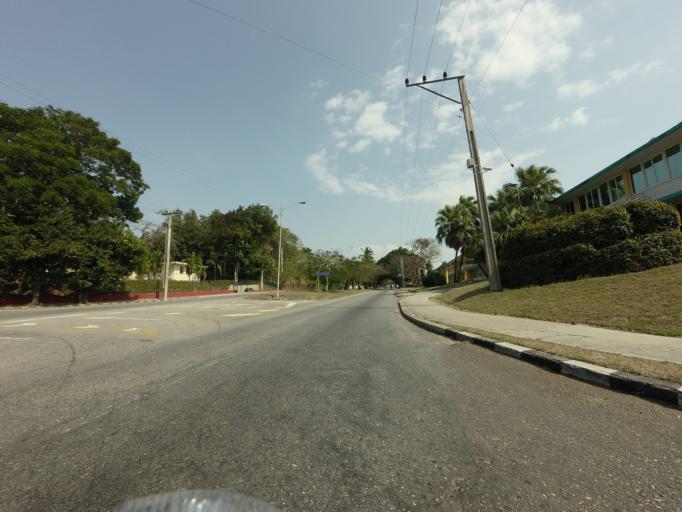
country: CU
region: La Habana
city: Cerro
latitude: 23.0783
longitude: -82.4589
